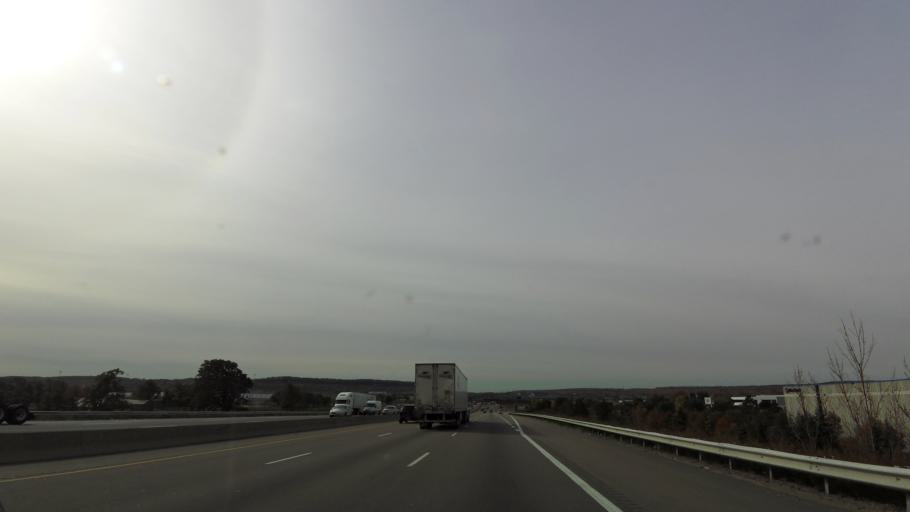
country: CA
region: Ontario
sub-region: Halton
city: Milton
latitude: 43.5316
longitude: -79.8978
